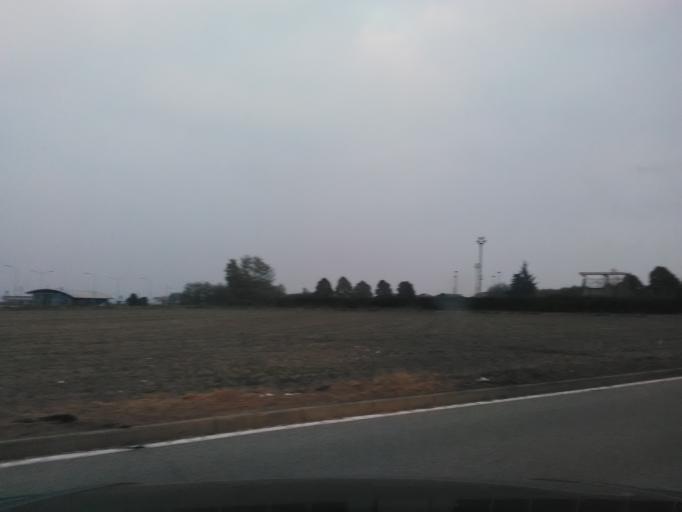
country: IT
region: Piedmont
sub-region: Provincia di Vercelli
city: Santhia
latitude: 45.3715
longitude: 8.1659
